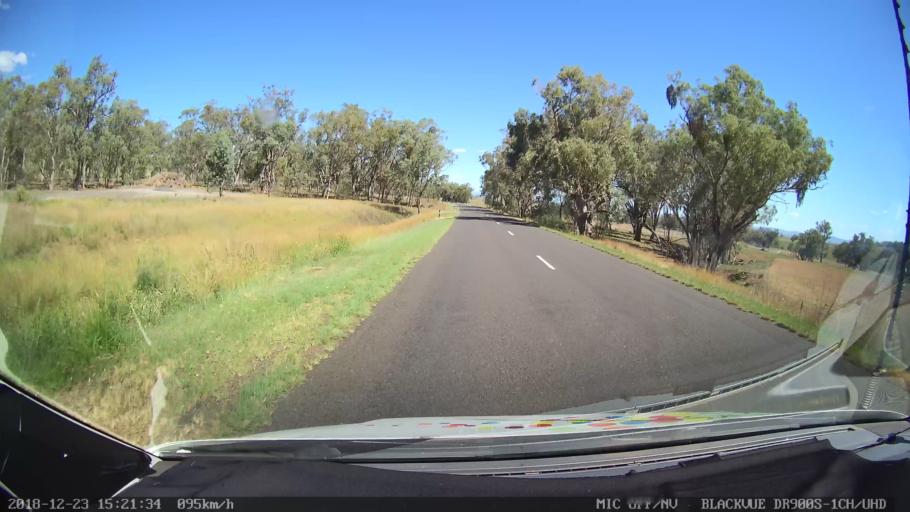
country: AU
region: New South Wales
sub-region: Tamworth Municipality
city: Manilla
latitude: -30.8581
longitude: 150.7975
